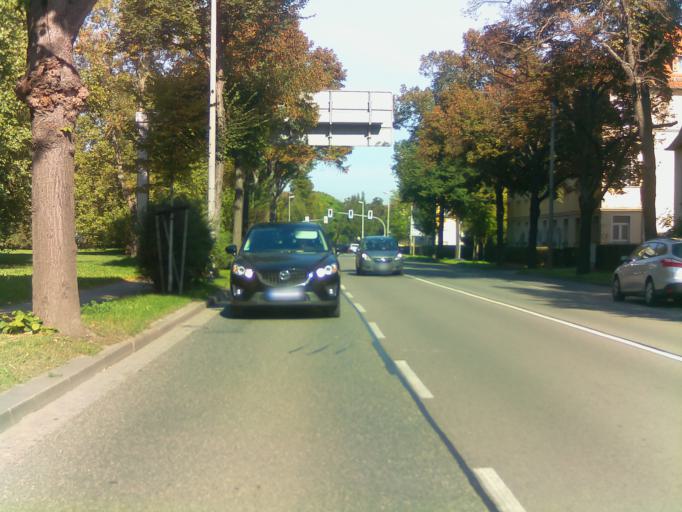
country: DE
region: Thuringia
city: Gera
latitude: 50.8729
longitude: 12.0732
